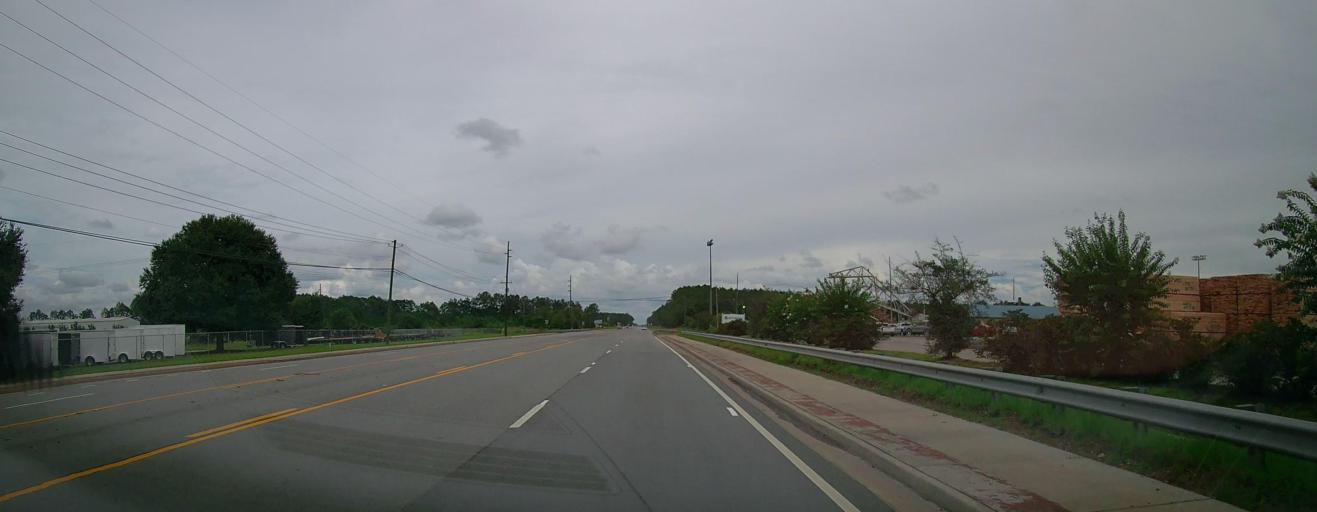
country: US
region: Georgia
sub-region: Appling County
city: Baxley
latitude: 31.7693
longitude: -82.3218
